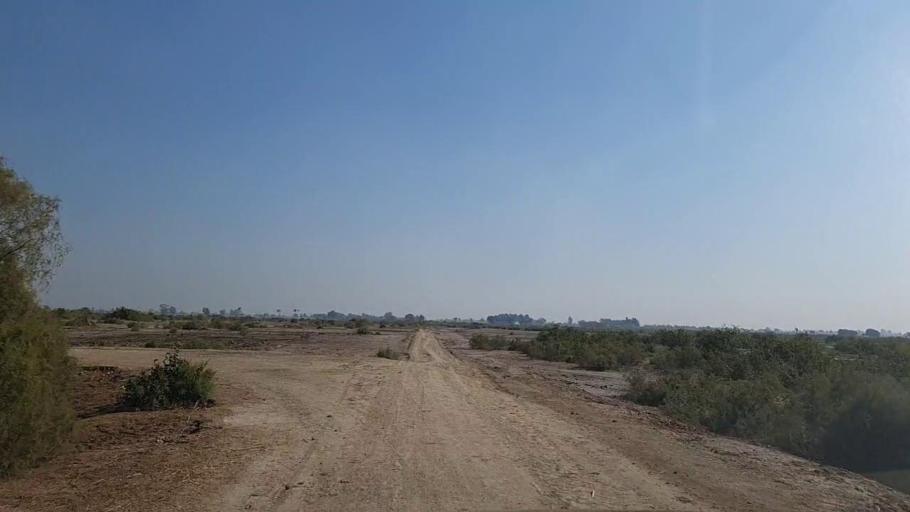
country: PK
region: Sindh
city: Nawabshah
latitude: 26.2962
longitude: 68.3840
